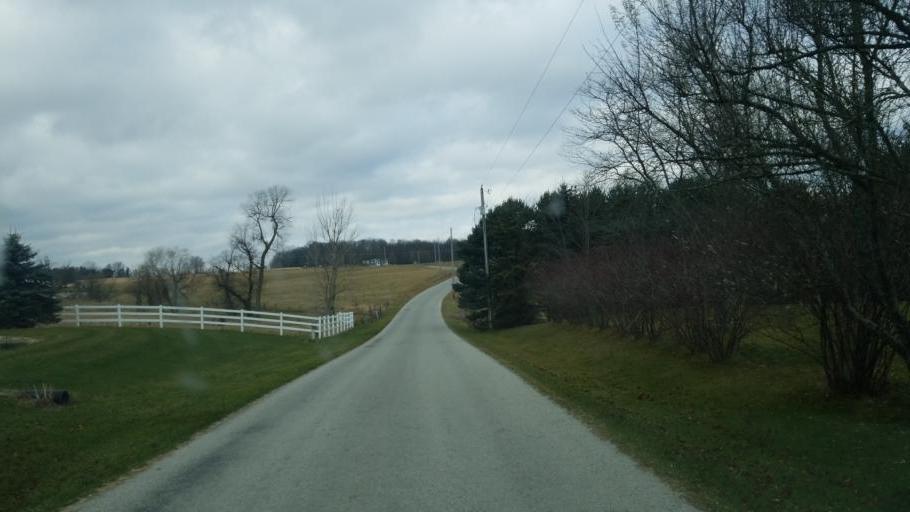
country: US
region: Ohio
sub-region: Crawford County
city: Galion
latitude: 40.6666
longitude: -82.7127
